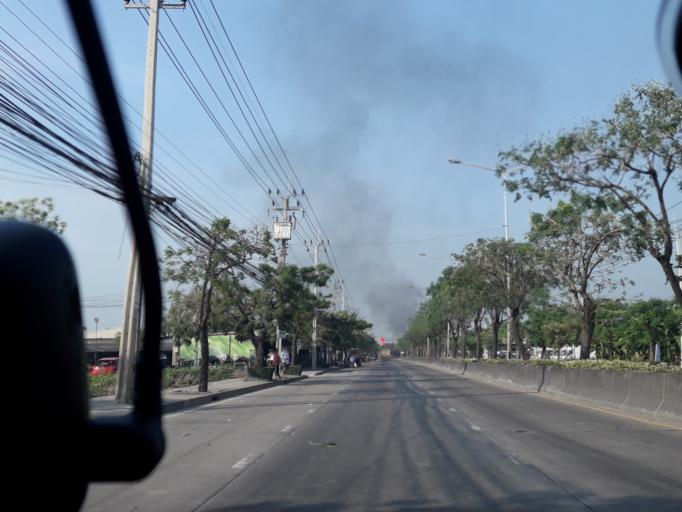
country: TH
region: Pathum Thani
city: Lam Luk Ka
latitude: 13.8892
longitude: 100.7317
